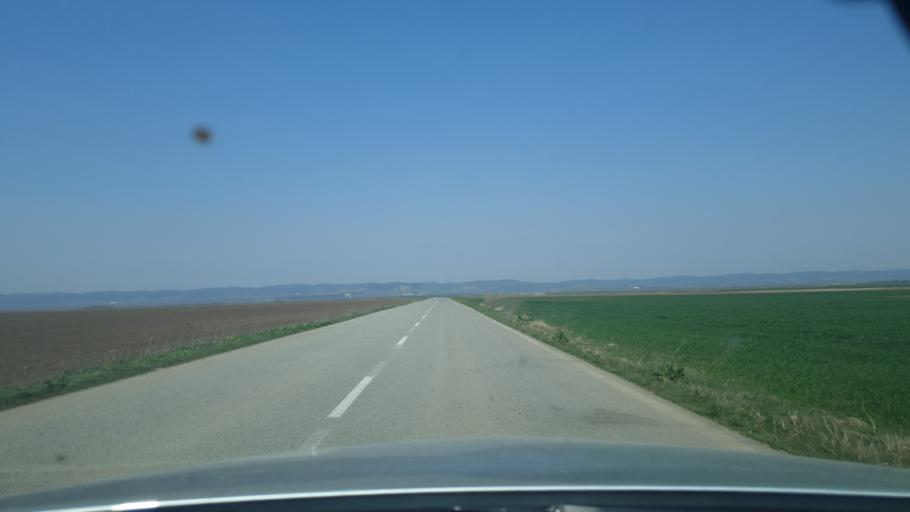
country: RS
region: Autonomna Pokrajina Vojvodina
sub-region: Sremski Okrug
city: Ruma
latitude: 45.0261
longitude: 19.7627
